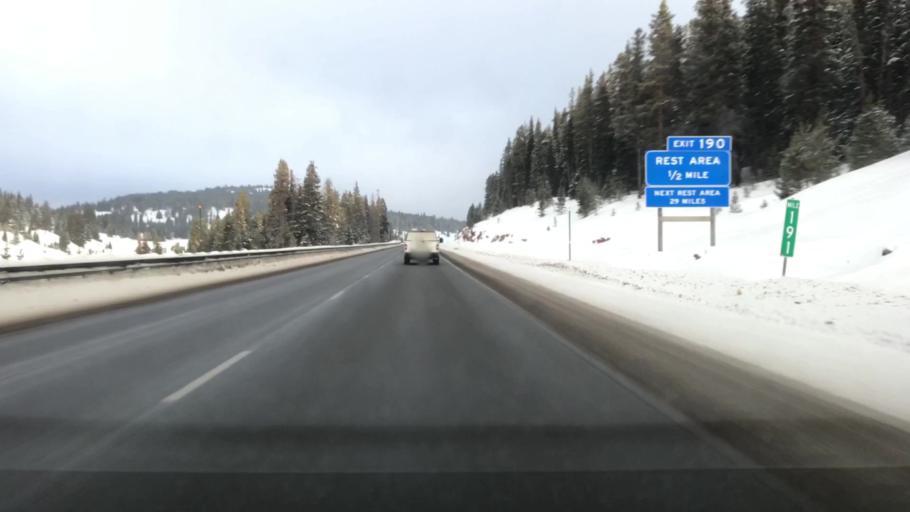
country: US
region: Colorado
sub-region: Summit County
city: Frisco
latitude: 39.5197
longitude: -106.2117
